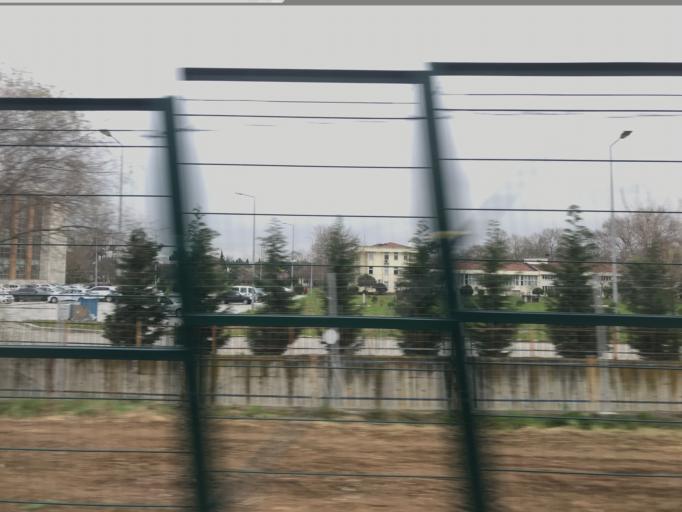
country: TR
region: Kocaeli
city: Darica
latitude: 40.8079
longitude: 29.3633
